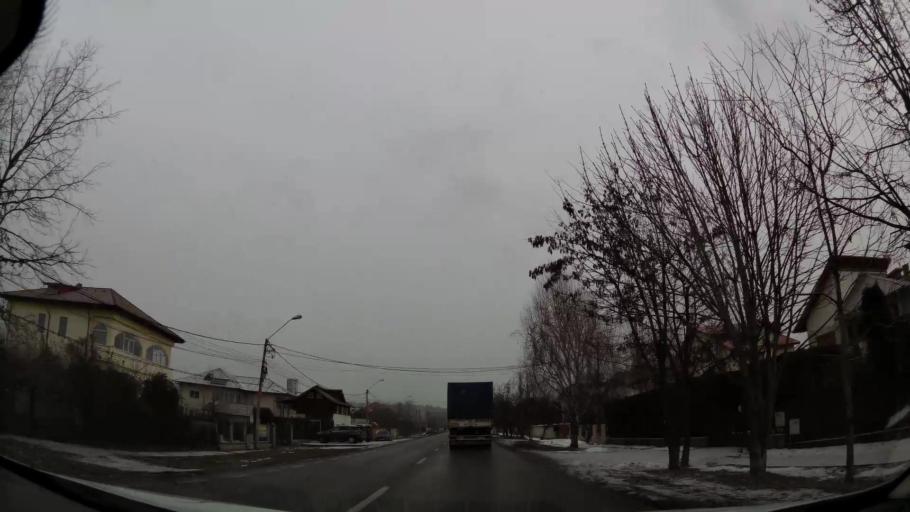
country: RO
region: Dambovita
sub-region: Comuna Aninoasa
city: Viforata
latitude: 44.9433
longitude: 25.4618
